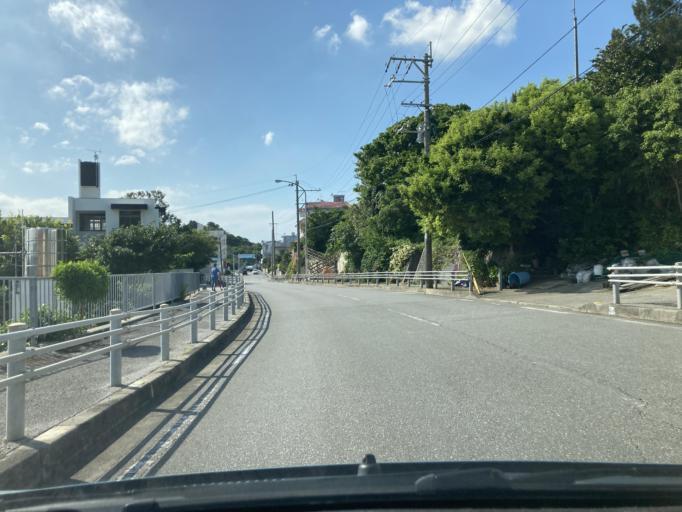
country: JP
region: Okinawa
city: Chatan
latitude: 26.2968
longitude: 127.7885
